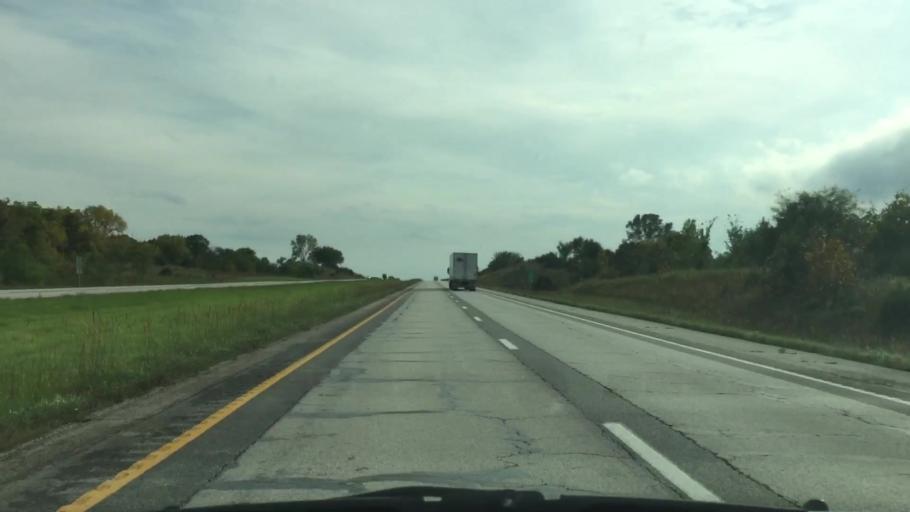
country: US
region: Missouri
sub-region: Harrison County
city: Bethany
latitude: 40.4459
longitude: -93.9830
